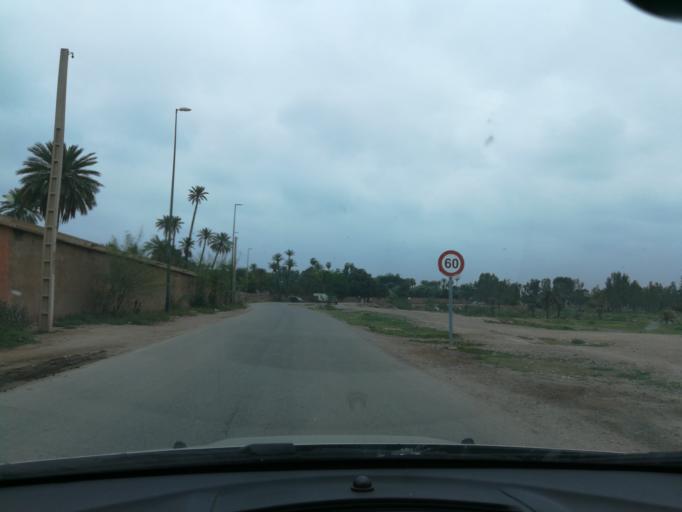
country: MA
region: Marrakech-Tensift-Al Haouz
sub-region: Marrakech
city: Marrakesh
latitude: 31.6617
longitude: -7.9834
